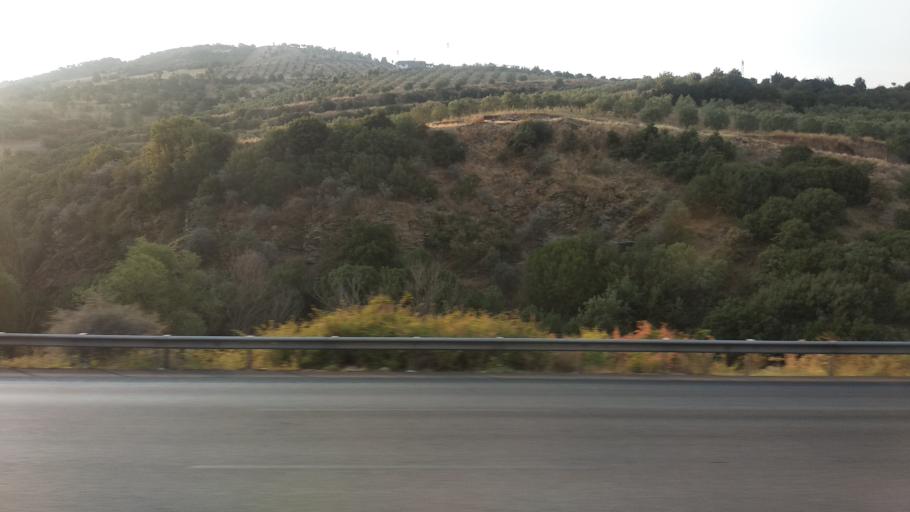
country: TR
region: Manisa
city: Menye
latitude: 38.5468
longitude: 28.4535
